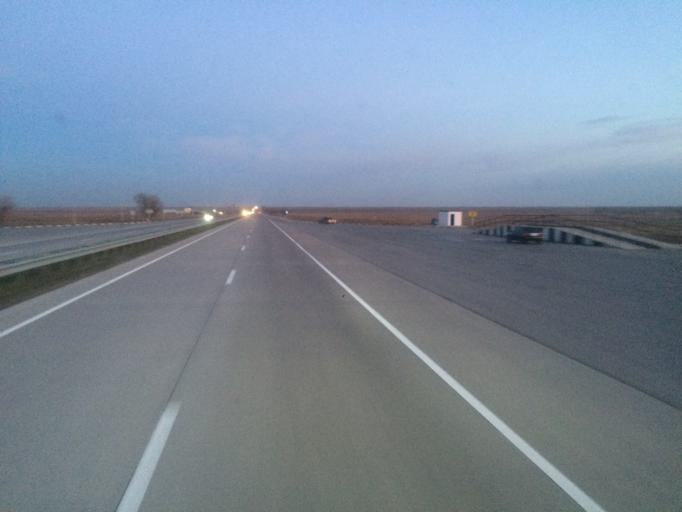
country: KZ
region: Ongtustik Qazaqstan
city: Temirlanovka
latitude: 42.8459
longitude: 69.0937
